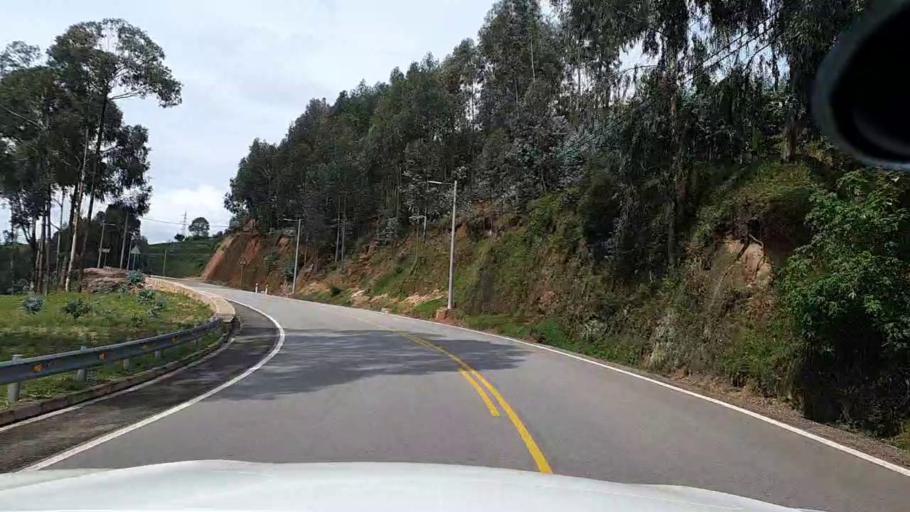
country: RW
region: Southern Province
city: Nzega
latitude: -2.5201
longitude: 29.4557
